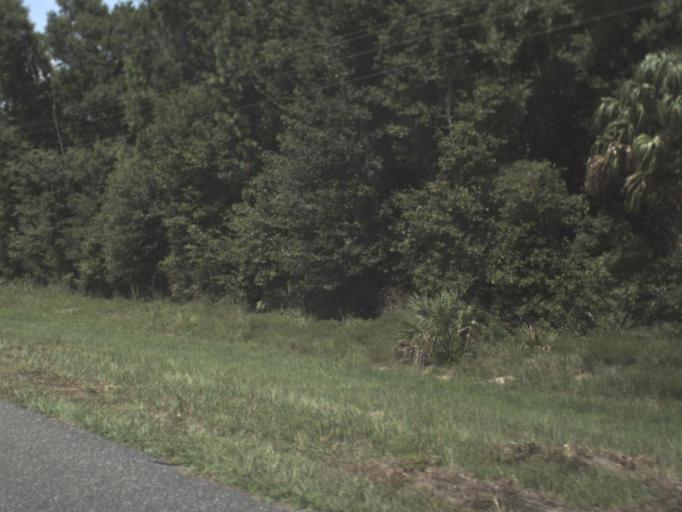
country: US
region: Florida
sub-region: Levy County
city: Inglis
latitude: 29.0962
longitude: -82.6359
